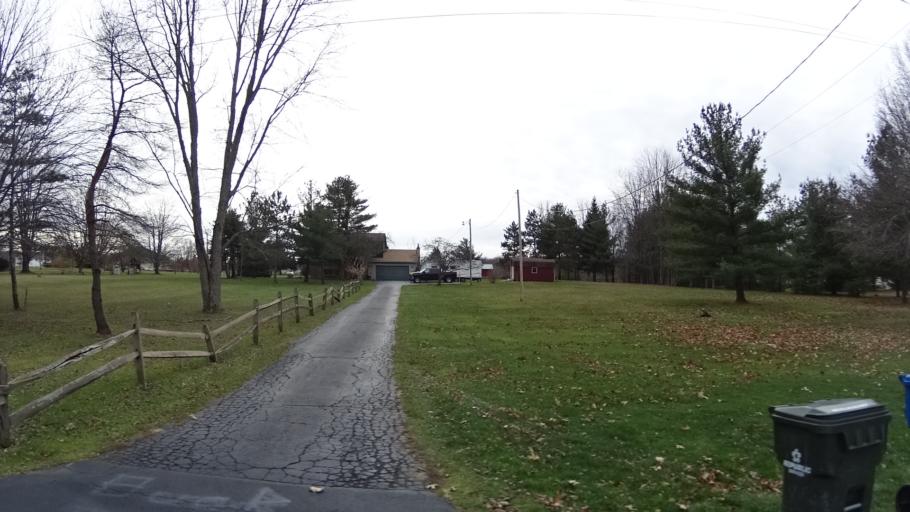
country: US
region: Ohio
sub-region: Lorain County
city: Wellington
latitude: 41.1998
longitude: -82.1705
